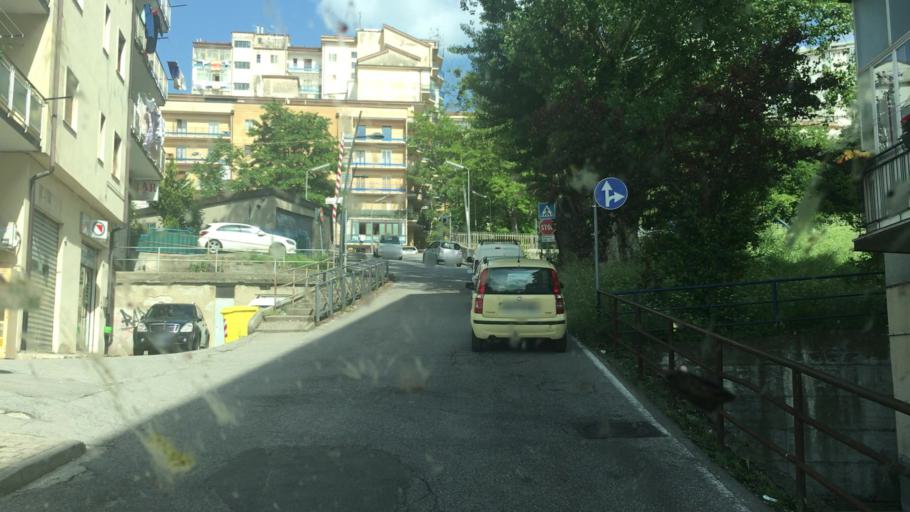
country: IT
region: Basilicate
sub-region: Provincia di Potenza
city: Potenza
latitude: 40.6422
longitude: 15.8027
